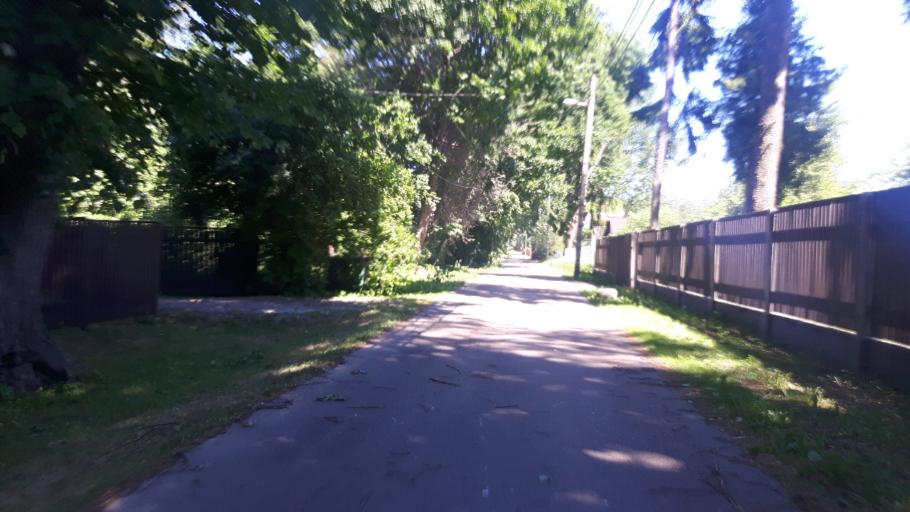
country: LV
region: Marupe
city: Marupe
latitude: 56.9497
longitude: 24.0315
